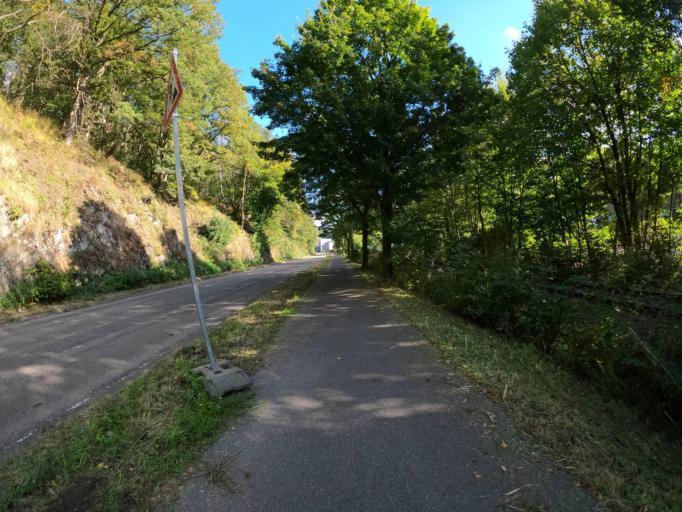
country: DE
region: North Rhine-Westphalia
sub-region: Regierungsbezirk Arnsberg
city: Schwelm
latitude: 51.2549
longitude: 7.2392
